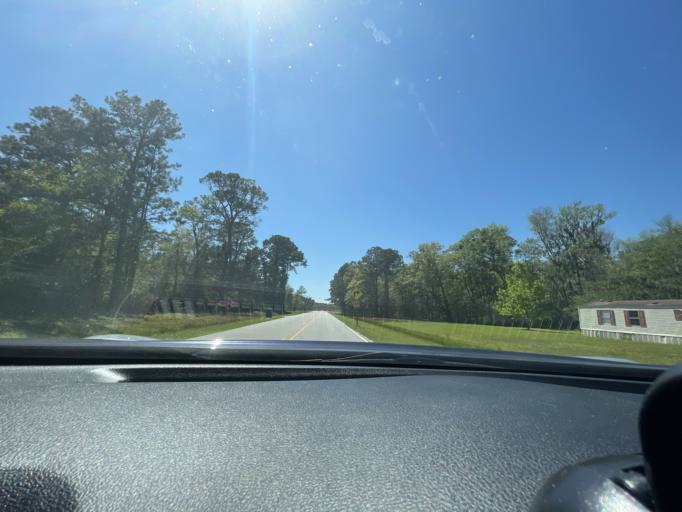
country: US
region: Georgia
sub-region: Chatham County
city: Bloomingdale
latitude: 32.0961
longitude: -81.2960
